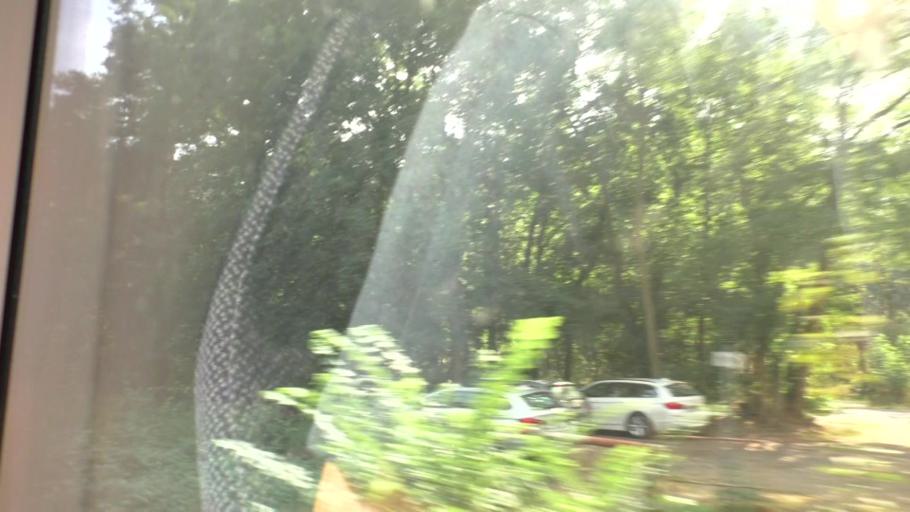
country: DE
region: Brandenburg
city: Wendisch Rietz
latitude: 52.2058
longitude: 14.0108
